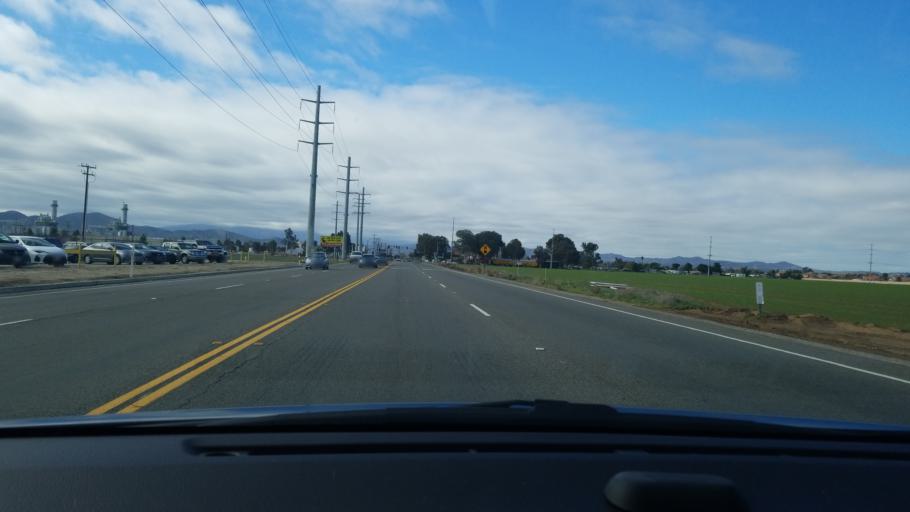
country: US
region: California
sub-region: Riverside County
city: Romoland
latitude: 33.7431
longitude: -117.1592
